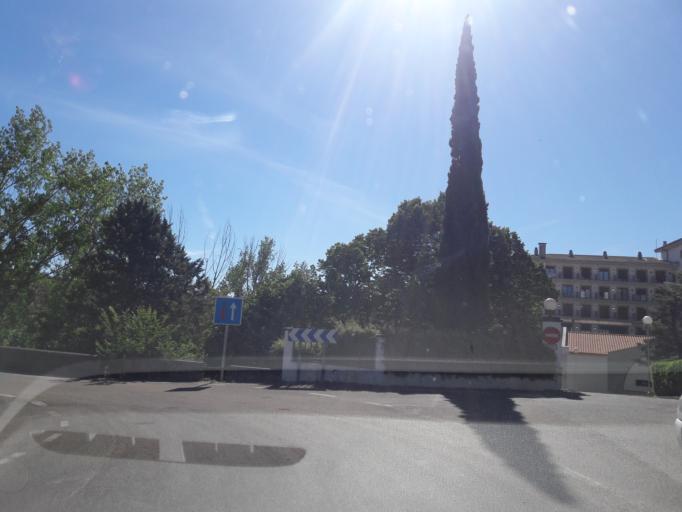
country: ES
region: Castille and Leon
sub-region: Provincia de Salamanca
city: Juzbado
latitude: 41.0706
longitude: -5.9010
